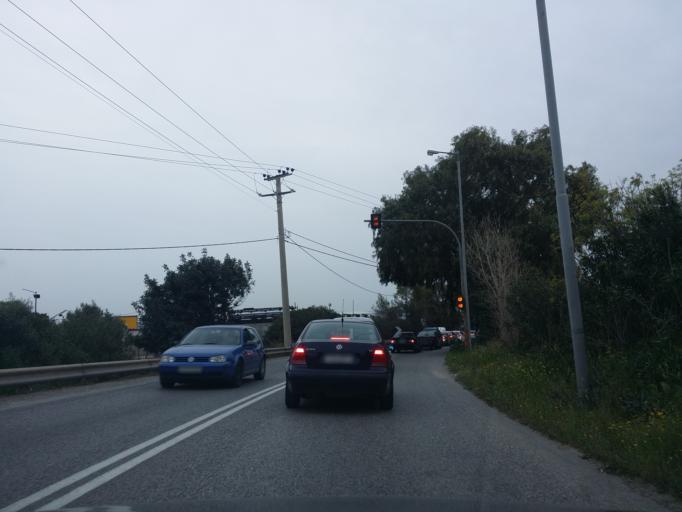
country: GR
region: Attica
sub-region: Nomarchia Dytikis Attikis
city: Mandra
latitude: 38.0769
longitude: 23.5071
